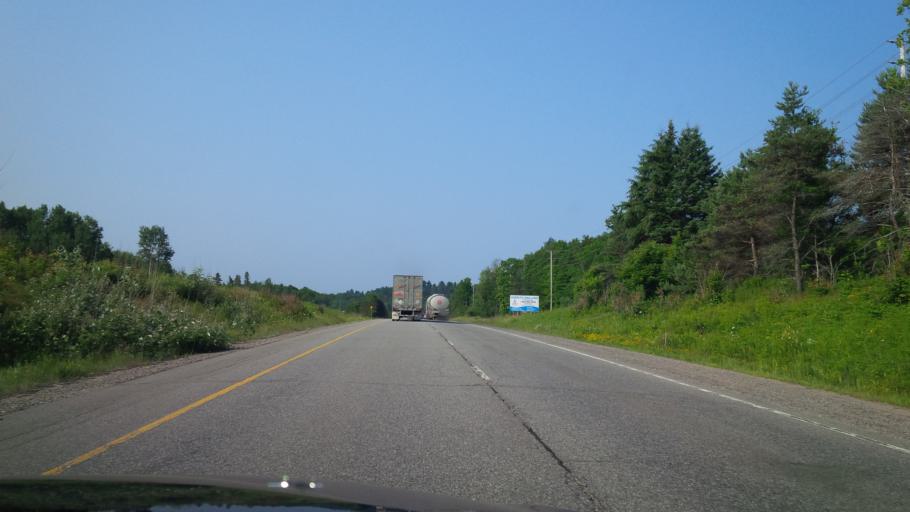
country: CA
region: Ontario
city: Huntsville
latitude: 45.2673
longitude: -79.2891
